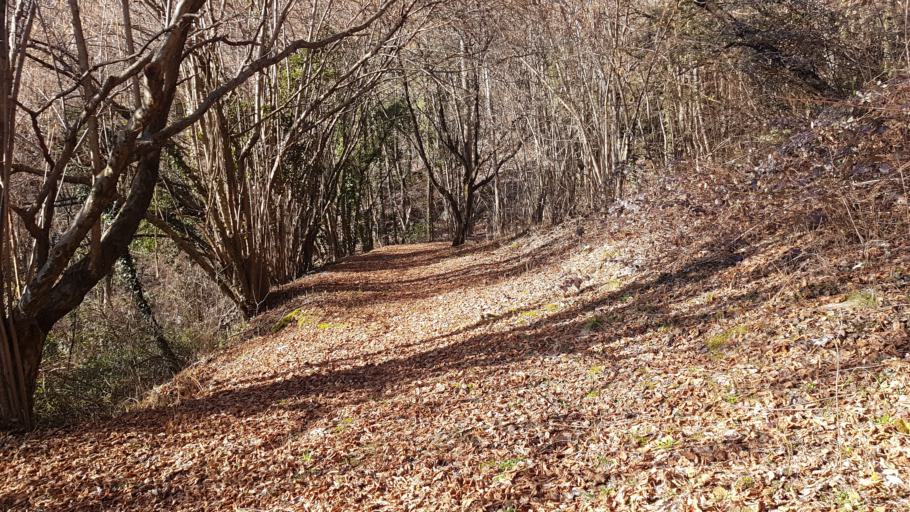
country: IT
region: Friuli Venezia Giulia
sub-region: Provincia di Udine
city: Torreano
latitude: 46.1719
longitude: 13.4254
